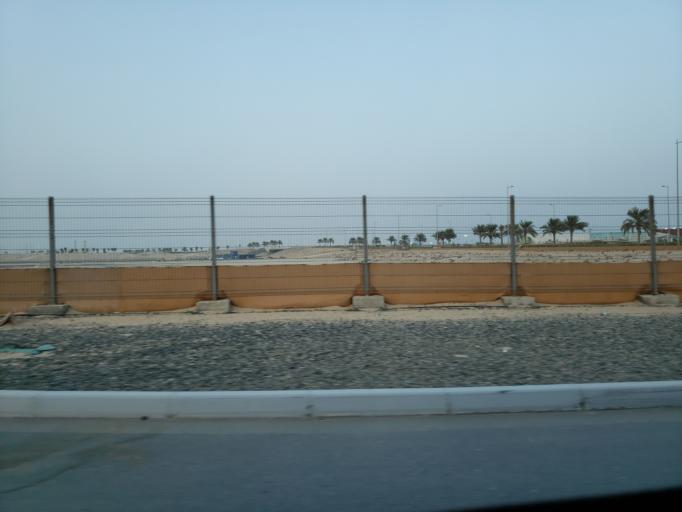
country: AE
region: Ajman
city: Ajman
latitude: 25.4295
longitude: 55.4608
